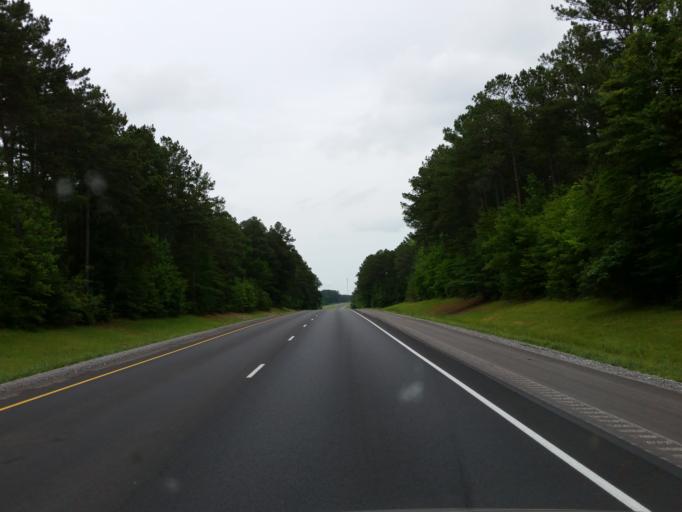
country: US
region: Mississippi
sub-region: Jones County
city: Sharon
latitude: 31.9512
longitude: -88.9800
